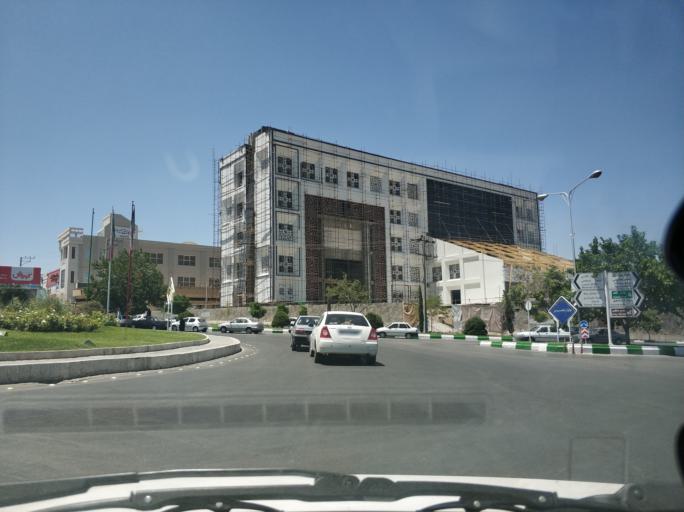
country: IR
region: Razavi Khorasan
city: Mashhad
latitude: 36.3143
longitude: 59.4901
